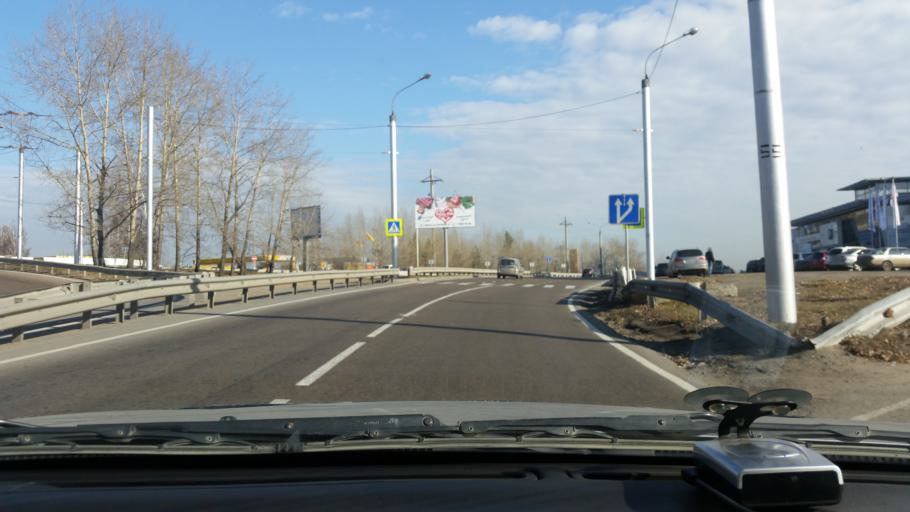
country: RU
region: Irkutsk
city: Dzerzhinsk
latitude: 52.2607
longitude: 104.3529
